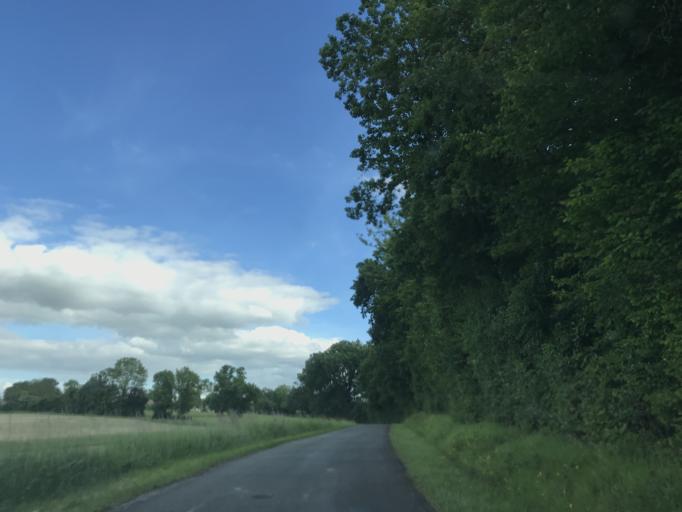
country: FR
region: Aquitaine
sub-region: Departement de la Dordogne
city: Saint-Aulaye
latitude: 45.2621
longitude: 0.1276
